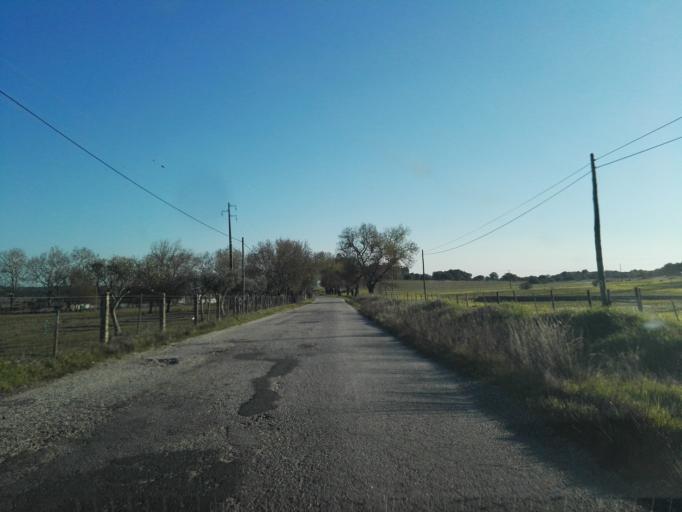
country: PT
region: Evora
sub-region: Evora
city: Evora
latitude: 38.5323
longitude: -7.9500
